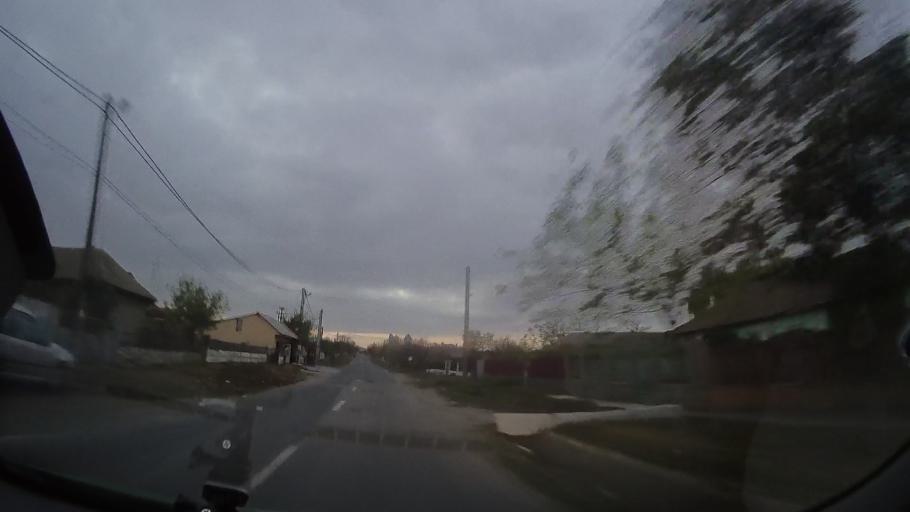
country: RO
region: Tulcea
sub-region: Comuna Mihai Bravu
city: Turda
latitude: 44.9733
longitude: 28.6253
